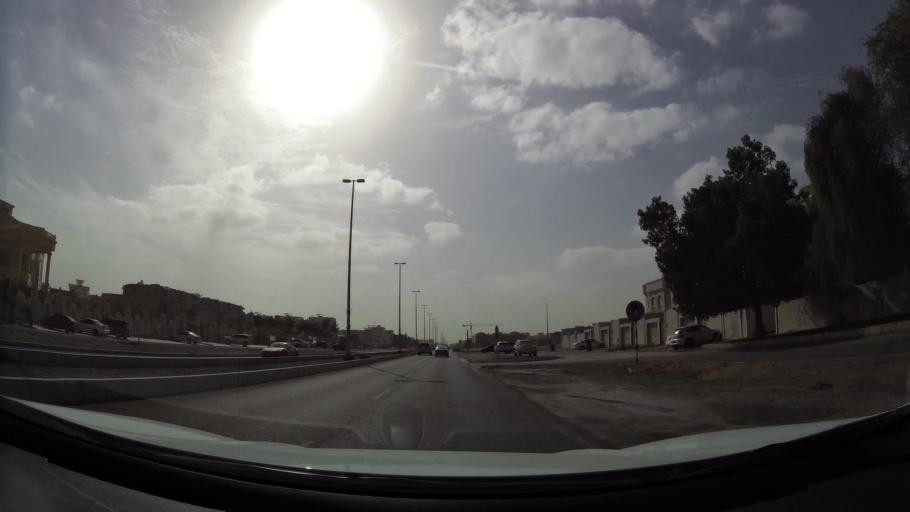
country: AE
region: Abu Dhabi
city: Abu Dhabi
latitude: 24.4173
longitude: 54.5798
